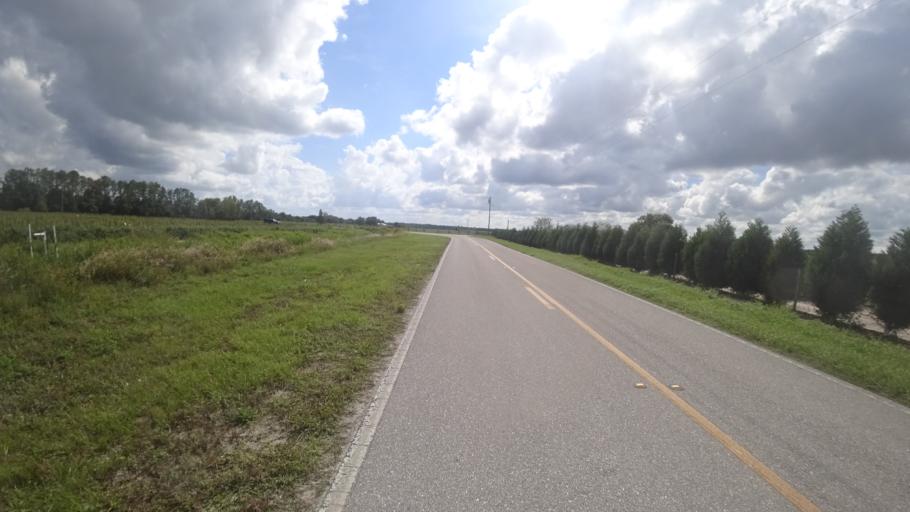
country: US
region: Florida
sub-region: Hillsborough County
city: Wimauma
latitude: 27.6127
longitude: -82.2312
